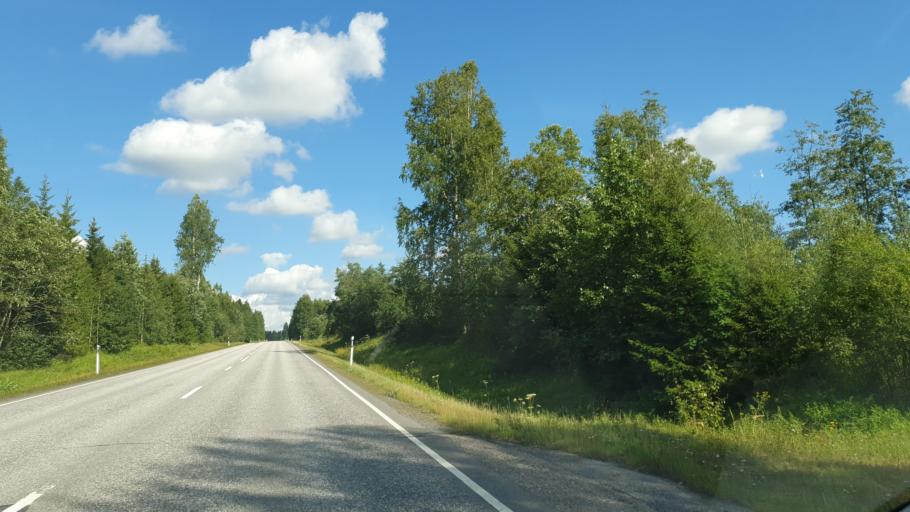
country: FI
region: Northern Savo
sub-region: Ylae-Savo
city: Sonkajaervi
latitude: 63.7355
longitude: 27.3784
